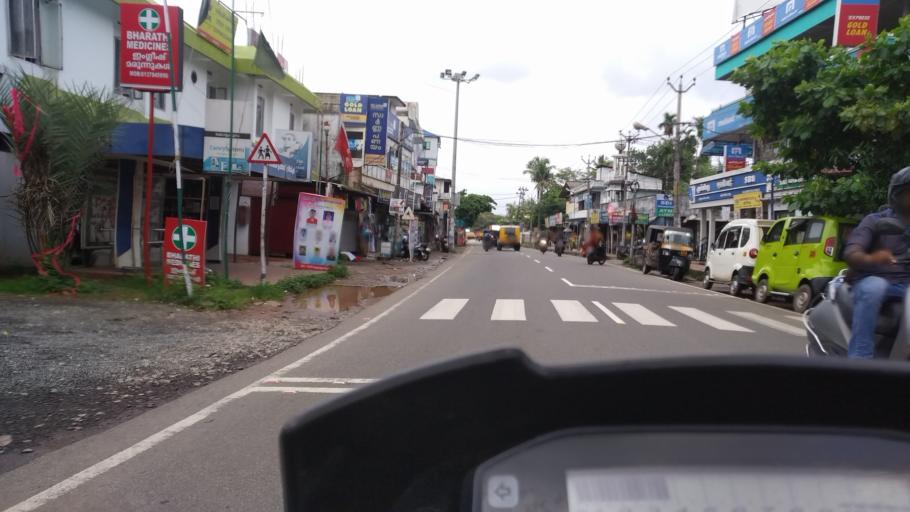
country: IN
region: Kerala
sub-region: Ernakulam
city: Aluva
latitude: 10.1291
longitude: 76.3000
